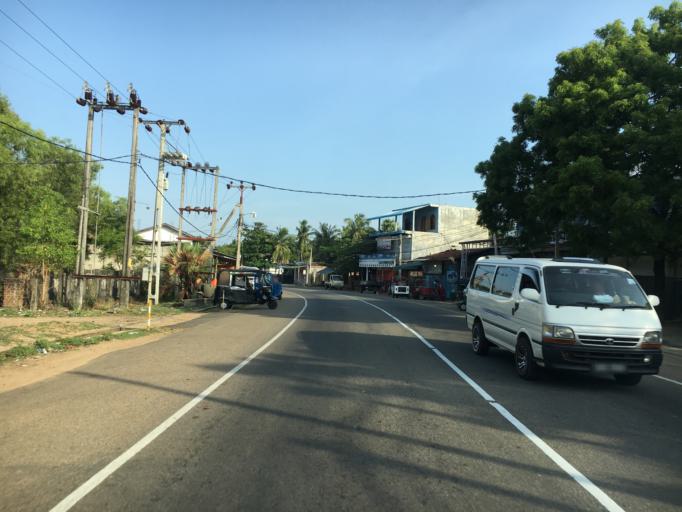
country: LK
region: Eastern Province
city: Eravur Town
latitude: 7.9103
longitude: 81.5301
